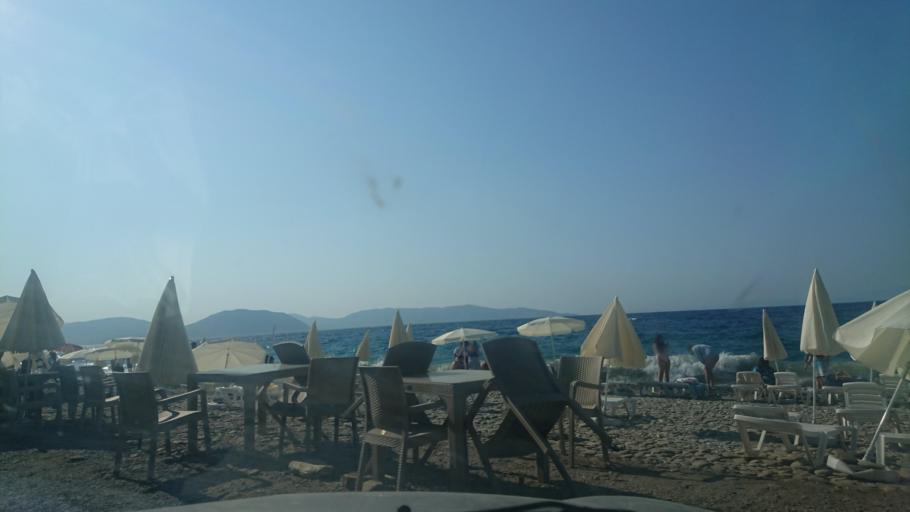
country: TR
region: Aydin
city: Atburgazi
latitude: 37.6896
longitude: 27.1287
